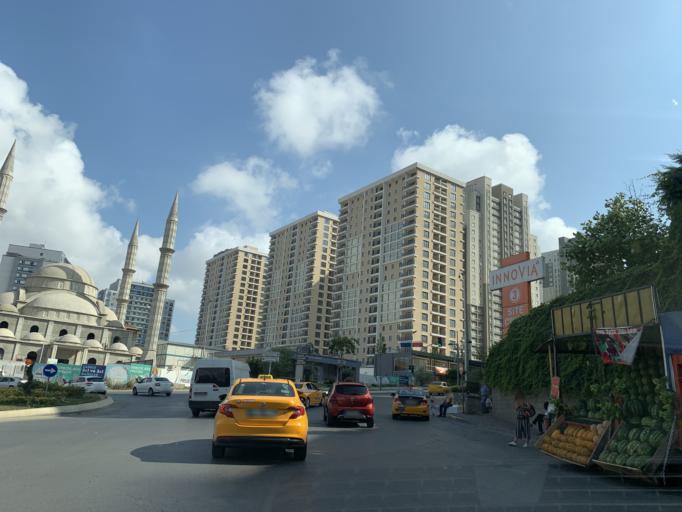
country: TR
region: Istanbul
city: Esenyurt
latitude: 41.0247
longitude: 28.6587
